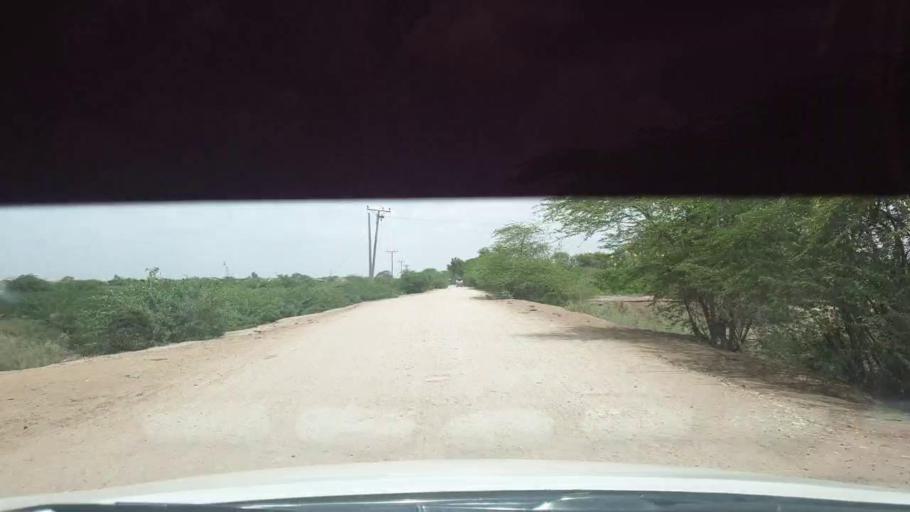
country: PK
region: Sindh
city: Kadhan
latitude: 24.4651
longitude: 69.0061
